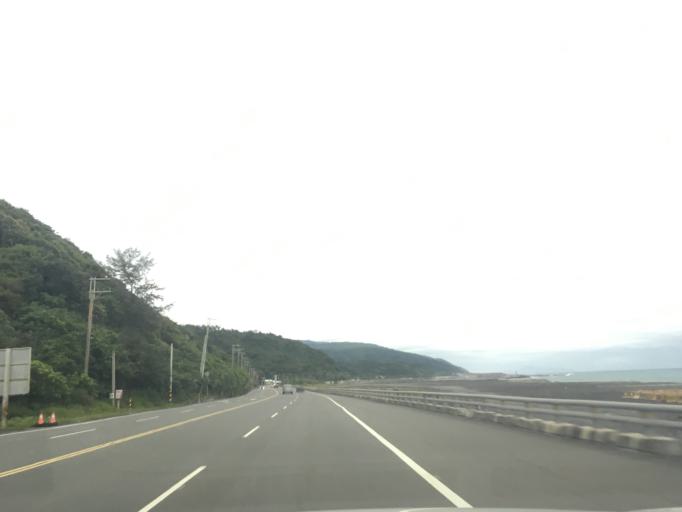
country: TW
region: Taiwan
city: Hengchun
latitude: 22.3246
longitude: 120.8921
